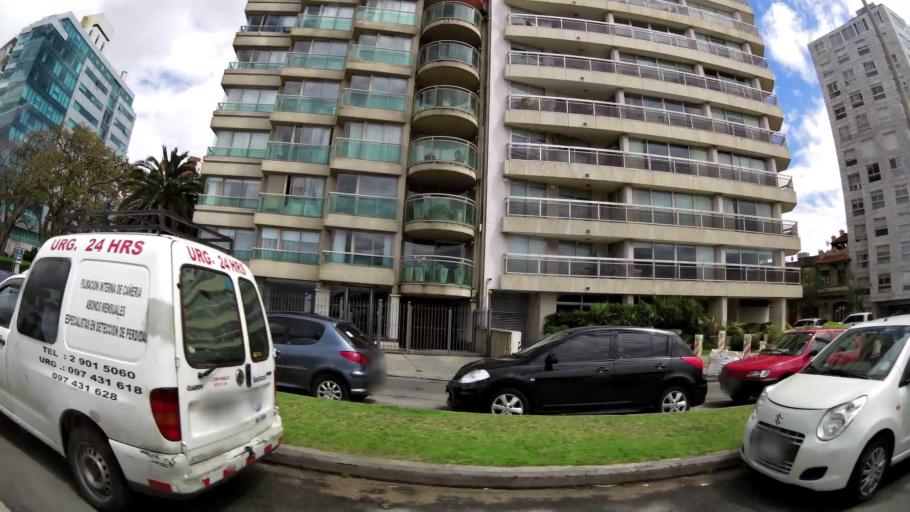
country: UY
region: Montevideo
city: Montevideo
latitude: -34.9278
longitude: -56.1589
